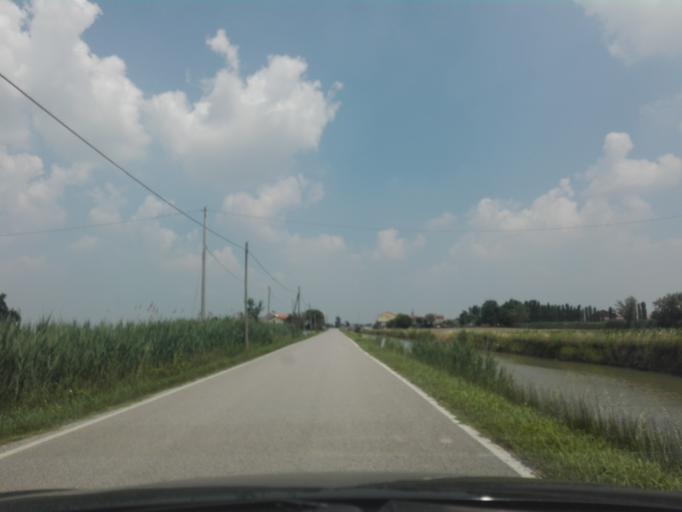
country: IT
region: Veneto
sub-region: Provincia di Rovigo
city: Gavello
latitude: 45.0106
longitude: 11.9130
